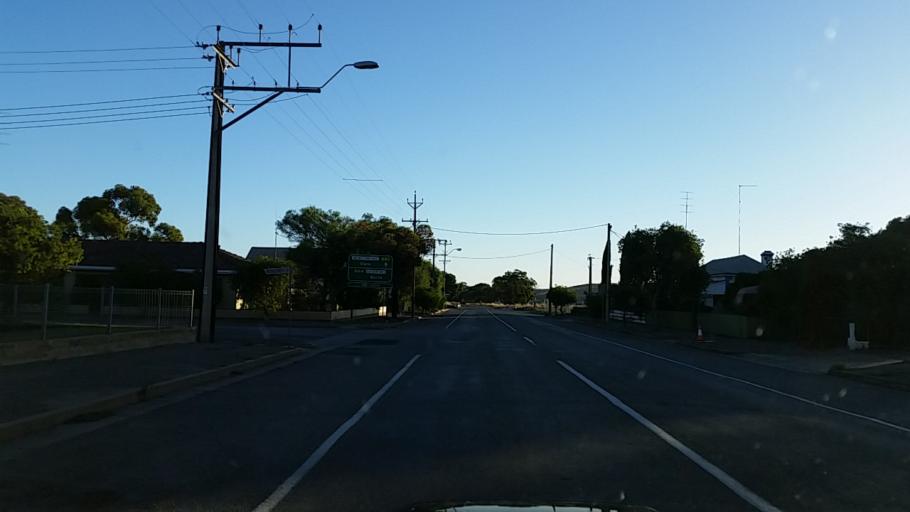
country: AU
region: South Australia
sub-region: Northern Areas
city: Jamestown
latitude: -33.4999
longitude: 138.6072
